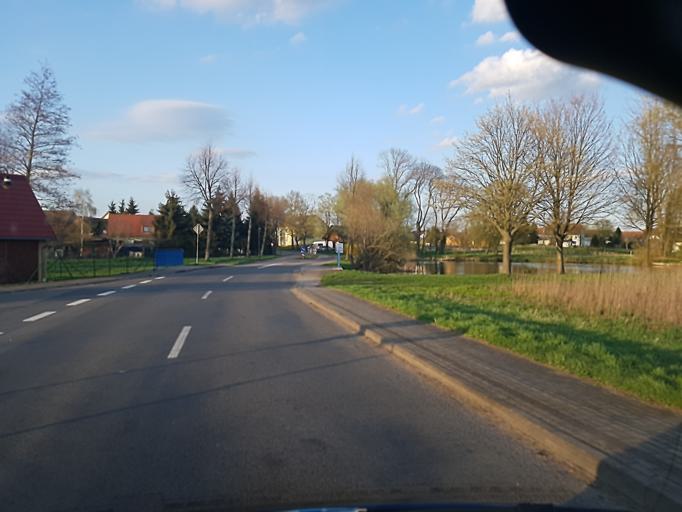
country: DE
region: Saxony
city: Trossin
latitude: 51.5665
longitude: 12.8447
